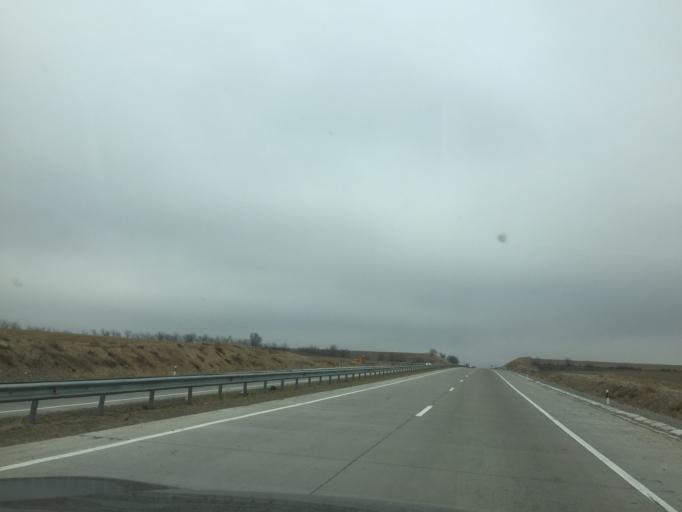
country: KZ
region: Ongtustik Qazaqstan
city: Aksu
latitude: 42.4759
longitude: 69.8886
